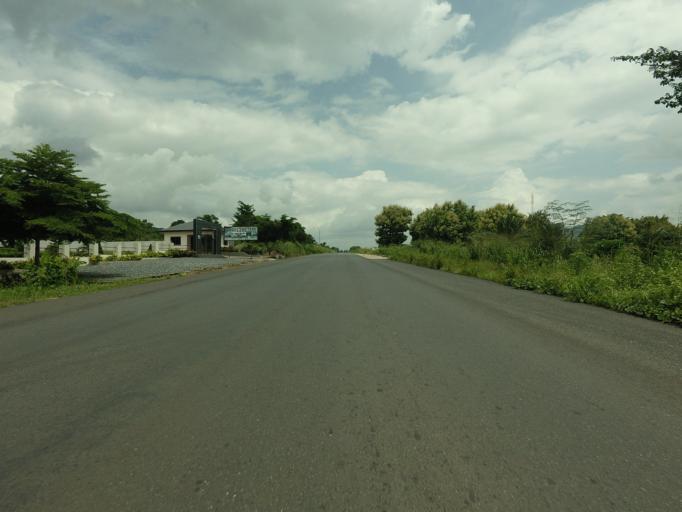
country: GH
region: Volta
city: Ho
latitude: 6.5557
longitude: 0.2597
